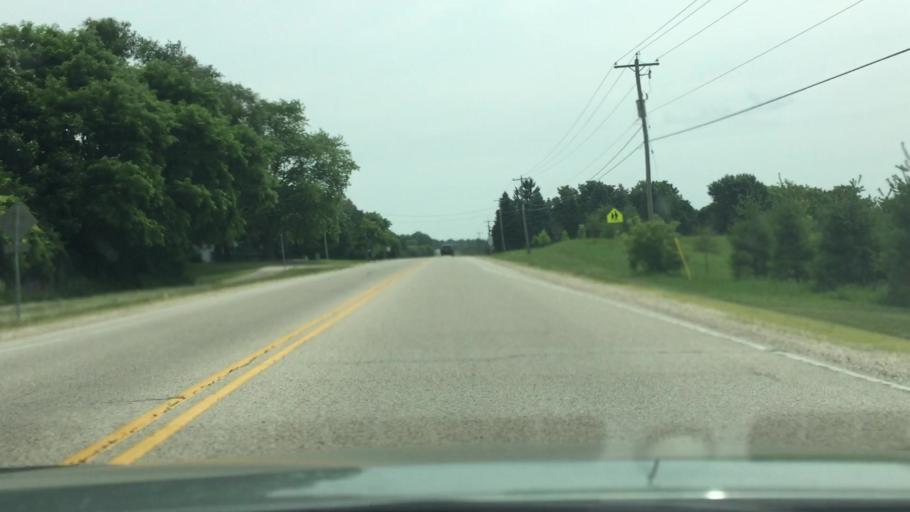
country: US
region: Wisconsin
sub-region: Waukesha County
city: Hartland
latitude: 43.0829
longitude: -88.3390
